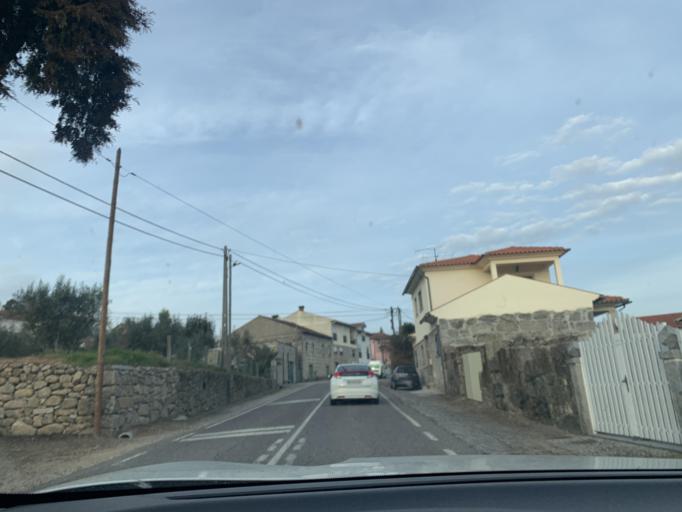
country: PT
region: Viseu
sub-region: Viseu
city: Viseu
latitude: 40.6053
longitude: -7.9816
